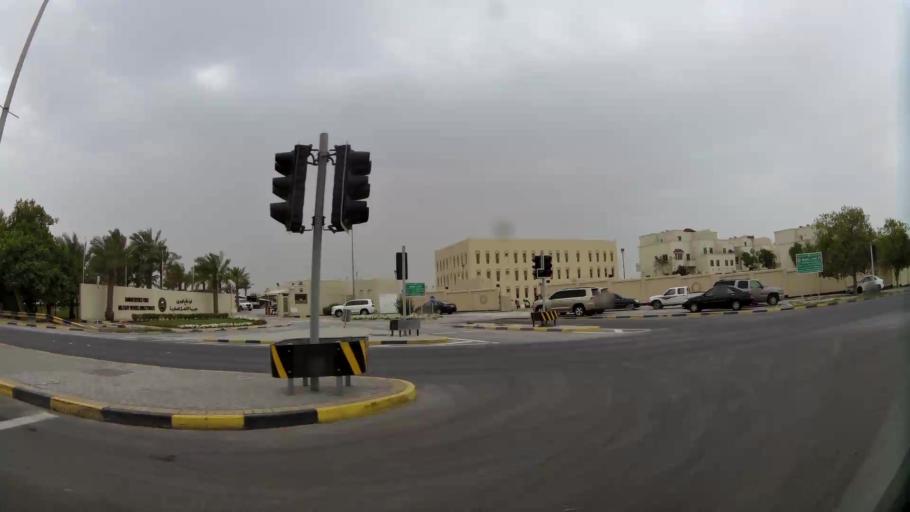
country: BH
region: Northern
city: Ar Rifa'
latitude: 26.1457
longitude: 50.5431
